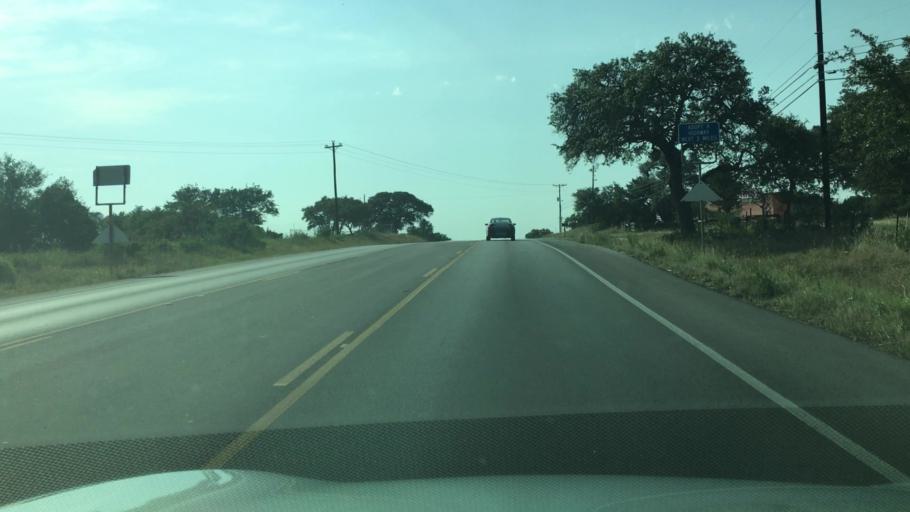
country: US
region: Texas
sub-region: Hays County
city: Wimberley
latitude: 29.9254
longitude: -98.0646
